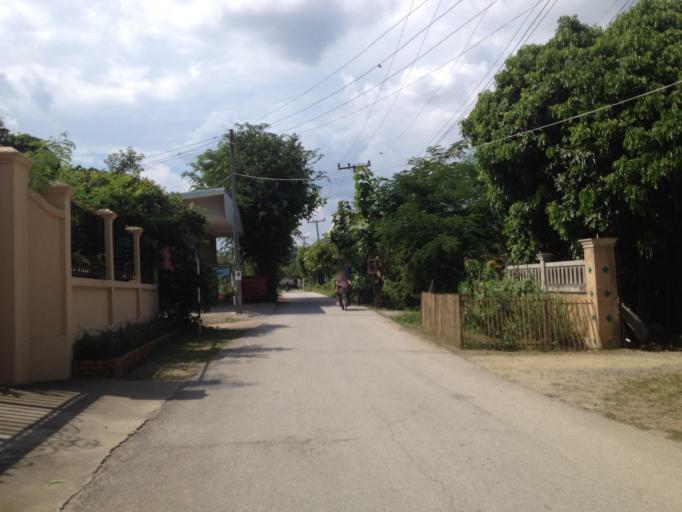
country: TH
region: Chiang Mai
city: Hang Dong
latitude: 18.7278
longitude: 98.9216
